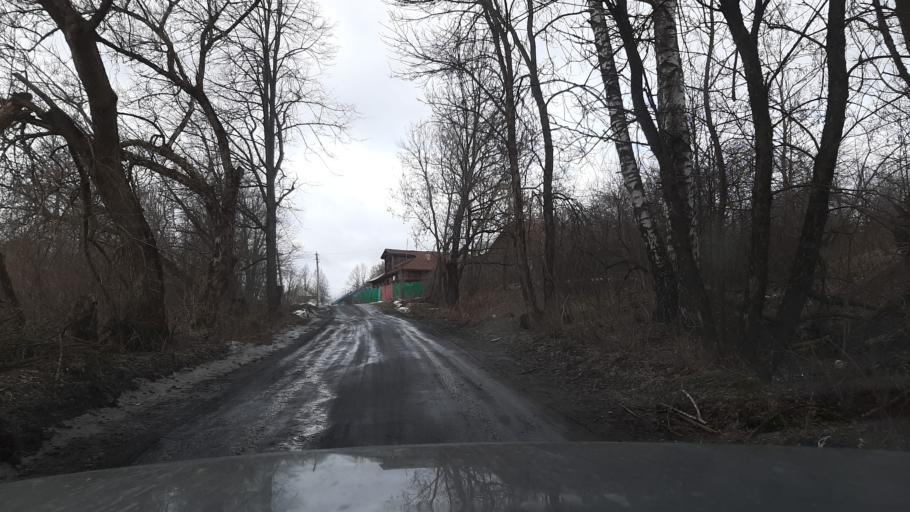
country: RU
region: Ivanovo
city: Teykovo
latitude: 56.8965
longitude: 40.6655
